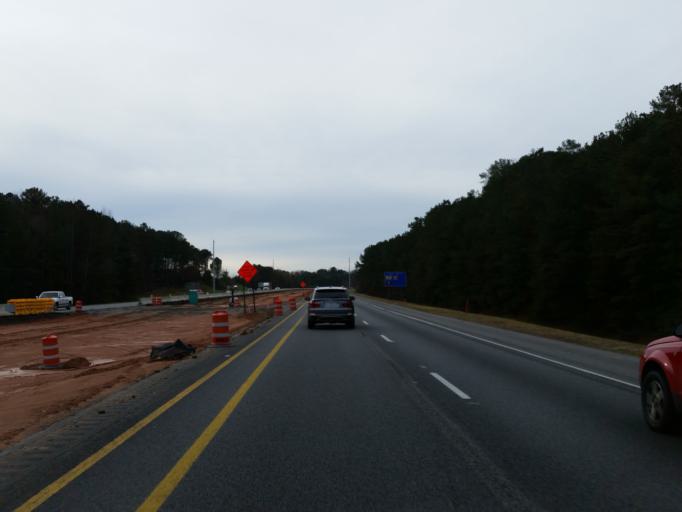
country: US
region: Georgia
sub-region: Cherokee County
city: Woodstock
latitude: 34.0649
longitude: -84.5411
